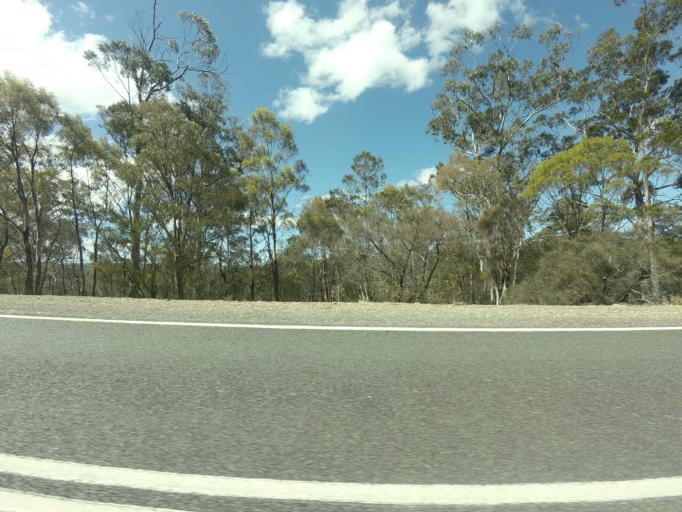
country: AU
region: Tasmania
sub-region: Break O'Day
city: St Helens
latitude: -42.0129
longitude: 147.9940
